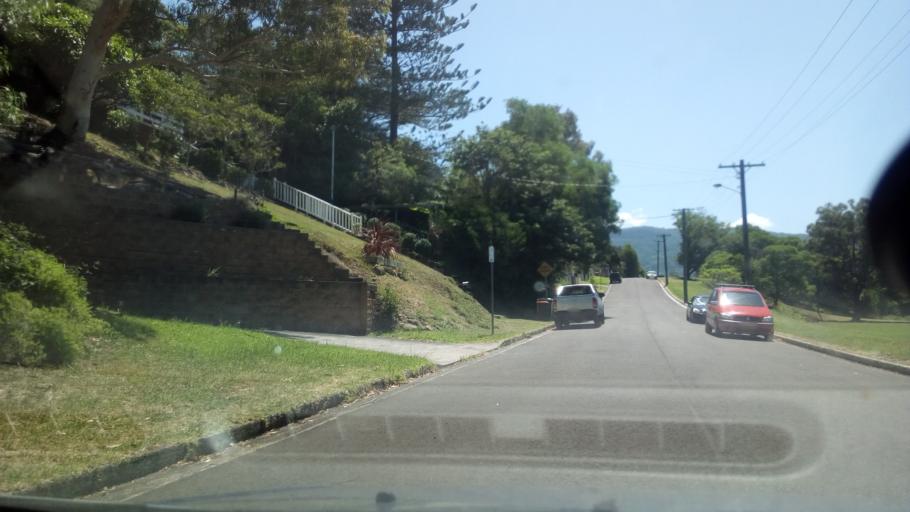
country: AU
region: New South Wales
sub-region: Wollongong
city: West Wollongong
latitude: -34.4305
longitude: 150.8599
